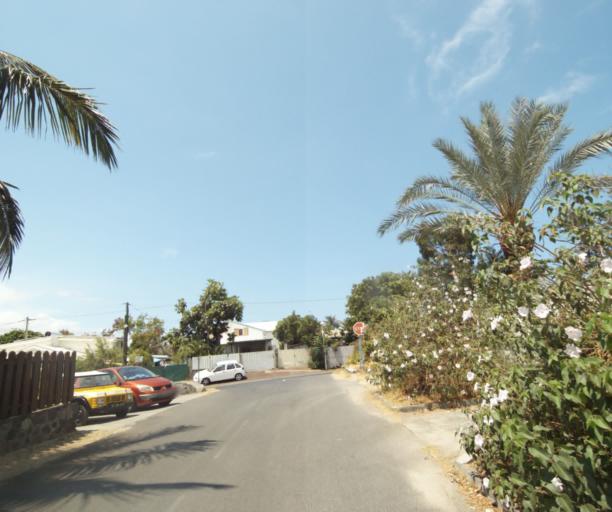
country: RE
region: Reunion
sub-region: Reunion
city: Trois-Bassins
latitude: -21.0804
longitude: 55.2283
